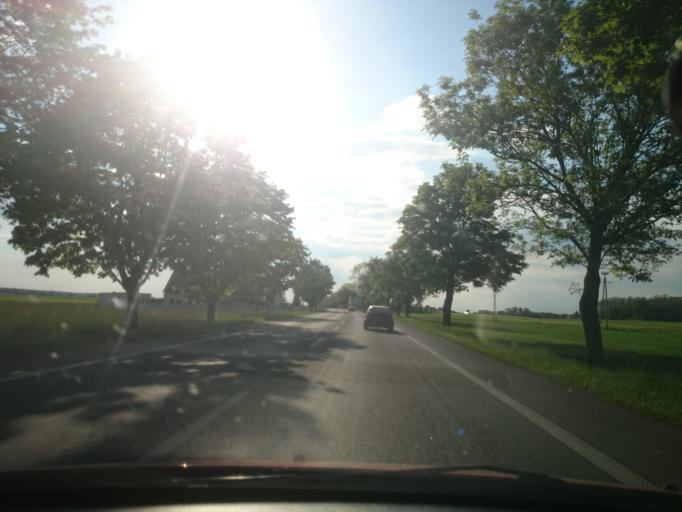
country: PL
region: Opole Voivodeship
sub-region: Powiat strzelecki
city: Izbicko
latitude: 50.5564
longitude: 18.2128
